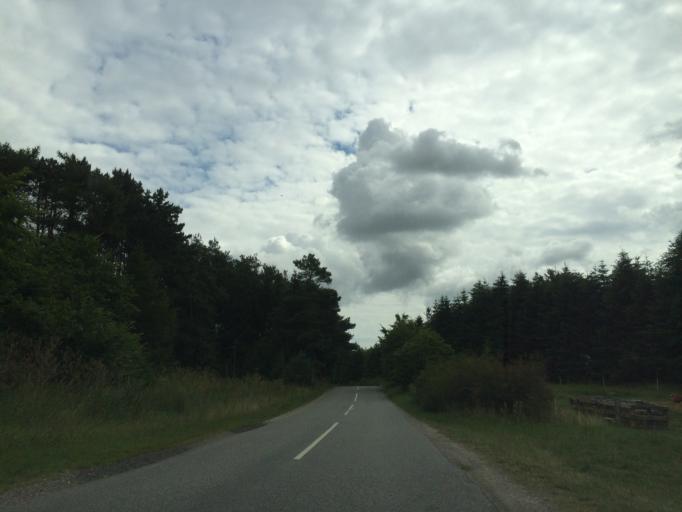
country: DK
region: Central Jutland
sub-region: Syddjurs Kommune
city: Ebeltoft
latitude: 56.2769
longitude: 10.6863
